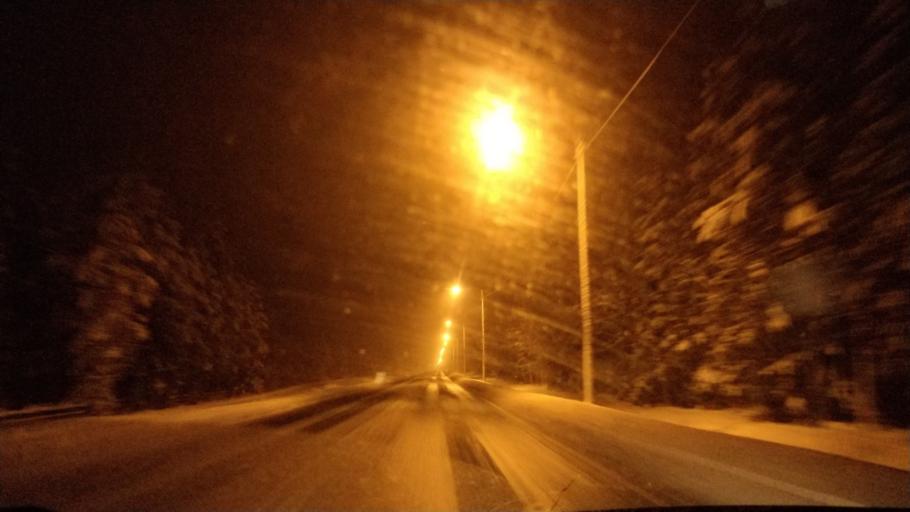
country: FI
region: Lapland
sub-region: Rovaniemi
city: Rovaniemi
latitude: 66.4137
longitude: 25.4092
